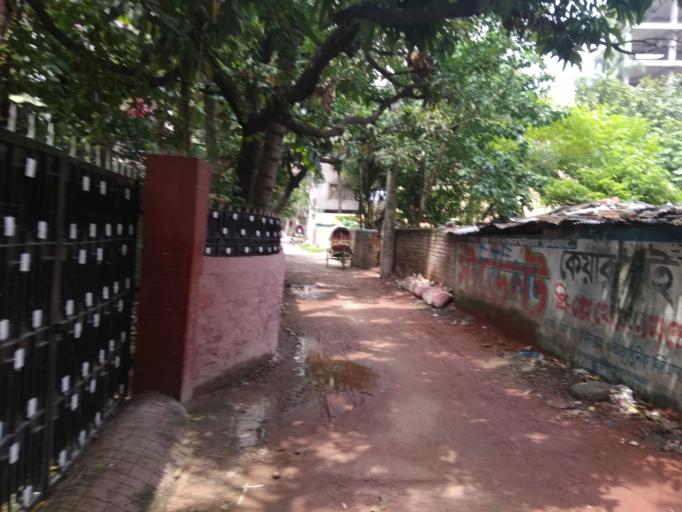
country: BD
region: Dhaka
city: Azimpur
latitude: 23.8020
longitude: 90.3652
